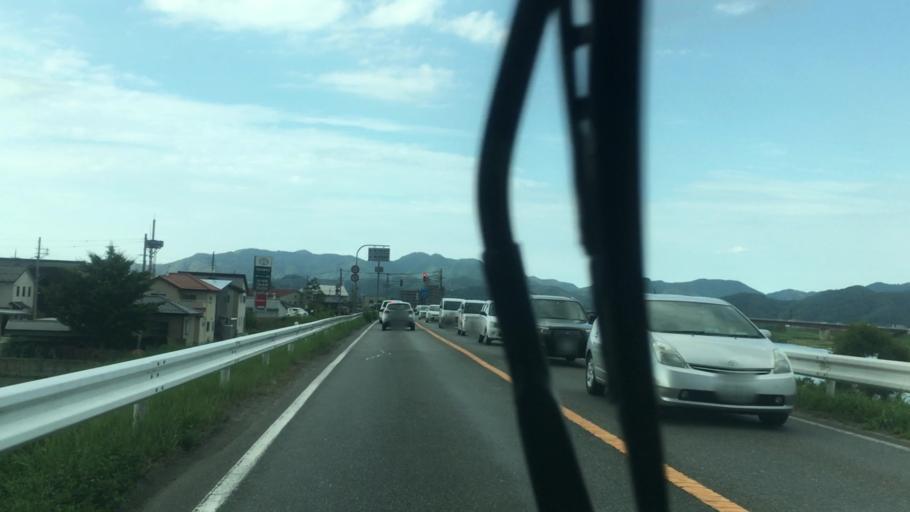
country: JP
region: Hyogo
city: Toyooka
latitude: 35.5221
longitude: 134.8219
